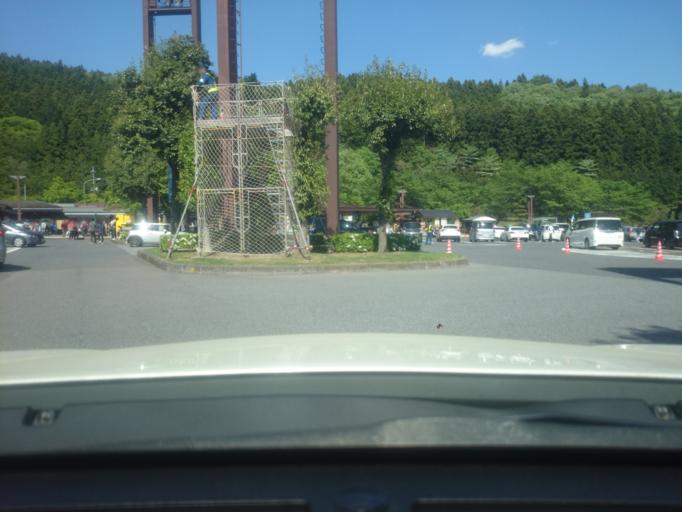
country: JP
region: Gunma
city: Annaka
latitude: 36.3411
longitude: 138.7396
